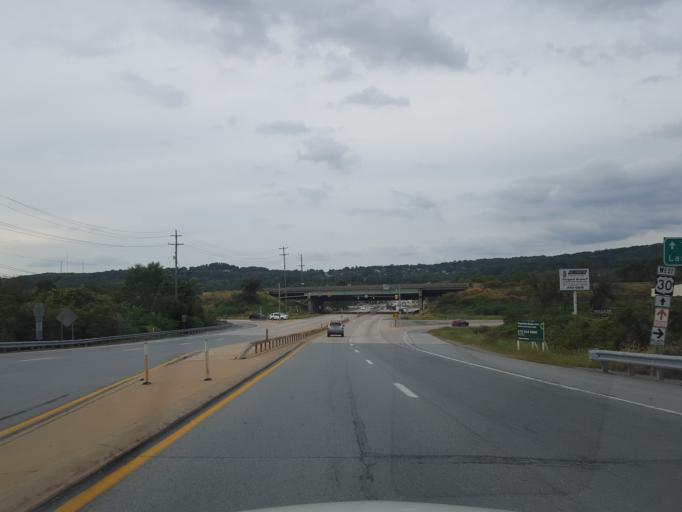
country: US
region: Pennsylvania
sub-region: York County
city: Yorklyn
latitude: 39.9844
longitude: -76.6659
